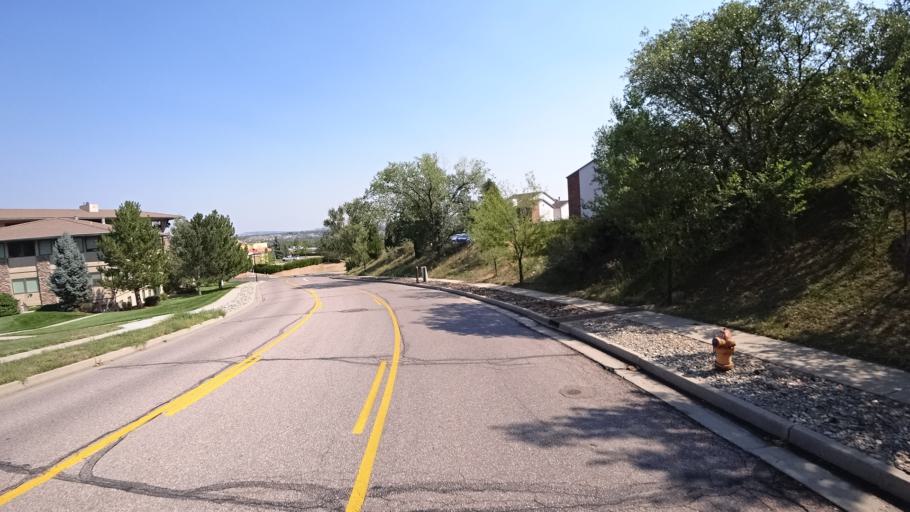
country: US
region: Colorado
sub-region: El Paso County
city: Stratmoor
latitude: 38.7947
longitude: -104.8123
